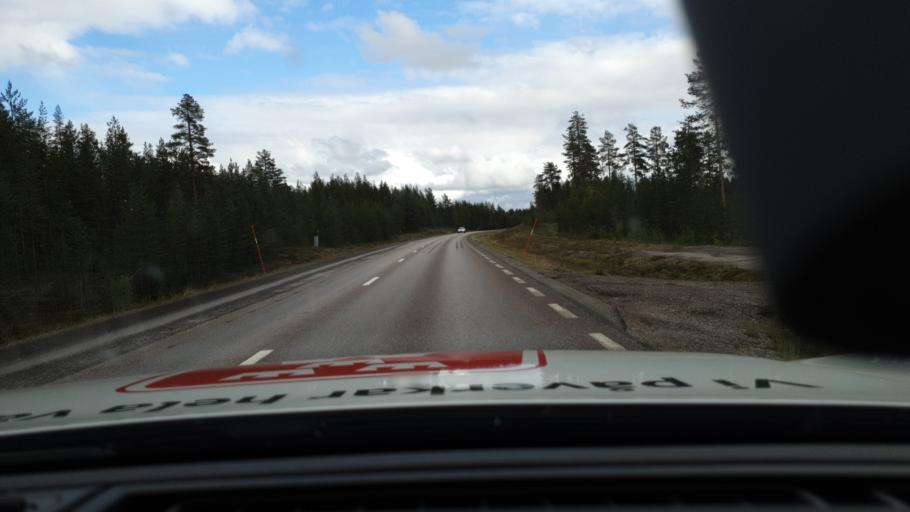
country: SE
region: Norrbotten
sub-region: Gallivare Kommun
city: Gaellivare
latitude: 66.9362
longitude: 21.4587
